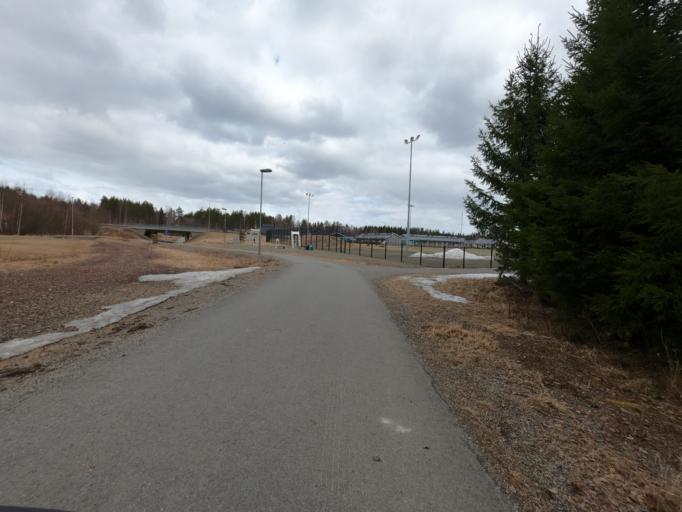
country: FI
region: North Karelia
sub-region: Joensuu
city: Joensuu
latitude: 62.5701
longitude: 29.8132
